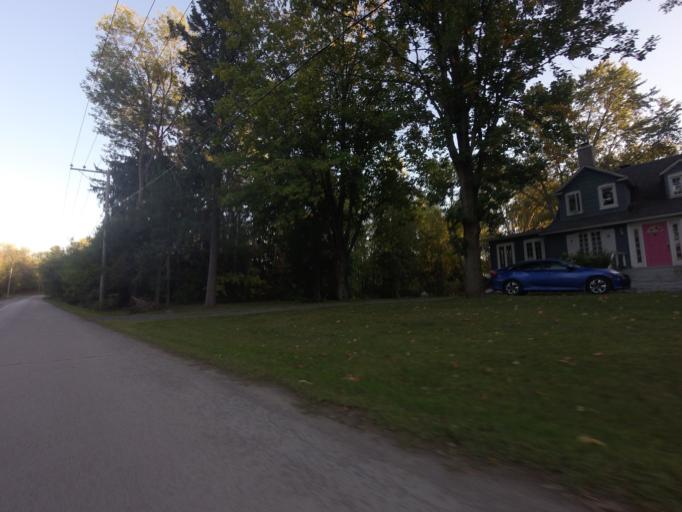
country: CA
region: Quebec
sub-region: Monteregie
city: Hudson
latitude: 45.4733
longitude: -74.1844
